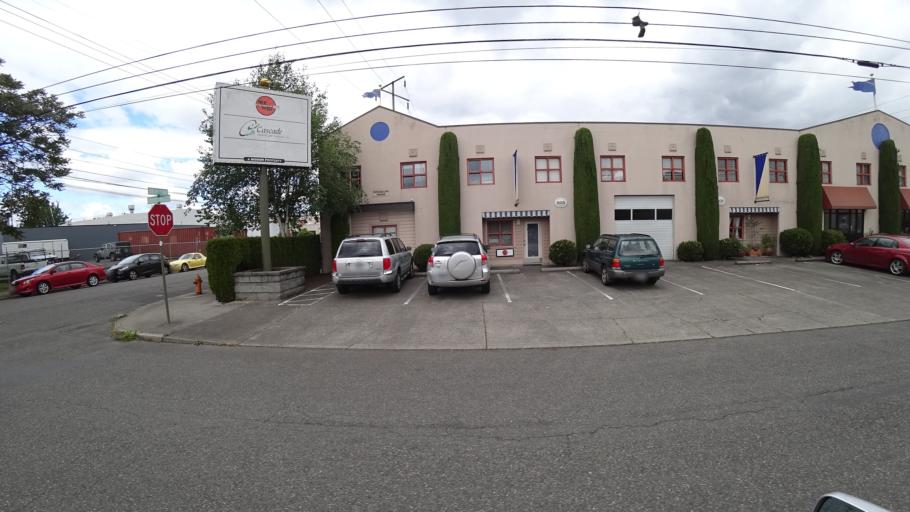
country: US
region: Oregon
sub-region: Multnomah County
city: Portland
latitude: 45.5065
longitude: -122.6577
